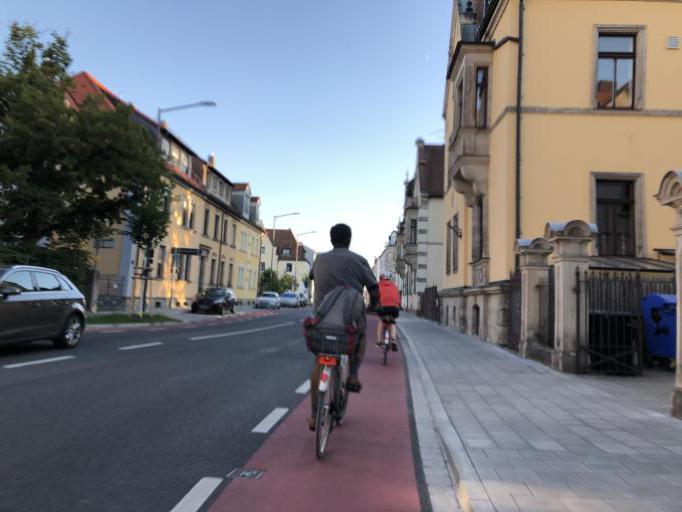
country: DE
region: Bavaria
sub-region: Regierungsbezirk Mittelfranken
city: Erlangen
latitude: 49.5987
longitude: 11.0184
